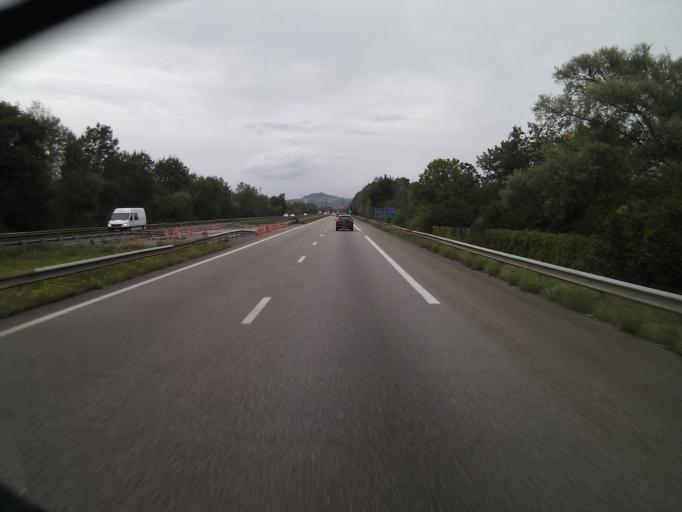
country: FR
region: Lorraine
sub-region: Departement de Meurthe-et-Moselle
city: Dieulouard
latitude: 48.8409
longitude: 6.0909
